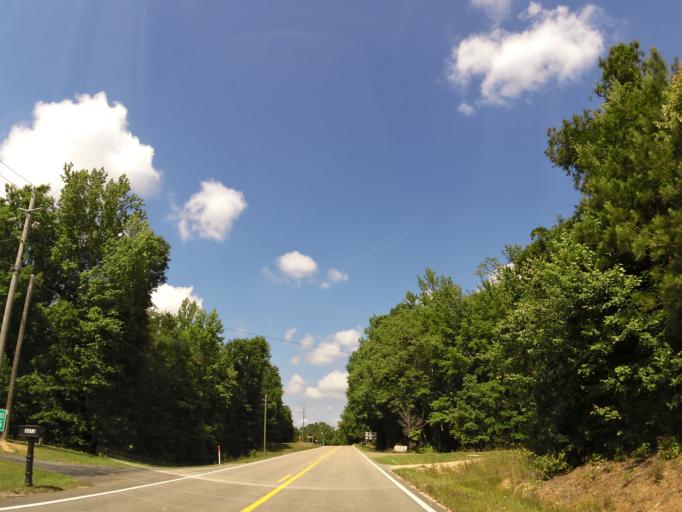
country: US
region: Alabama
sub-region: Marion County
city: Guin
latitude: 34.0095
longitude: -87.8499
